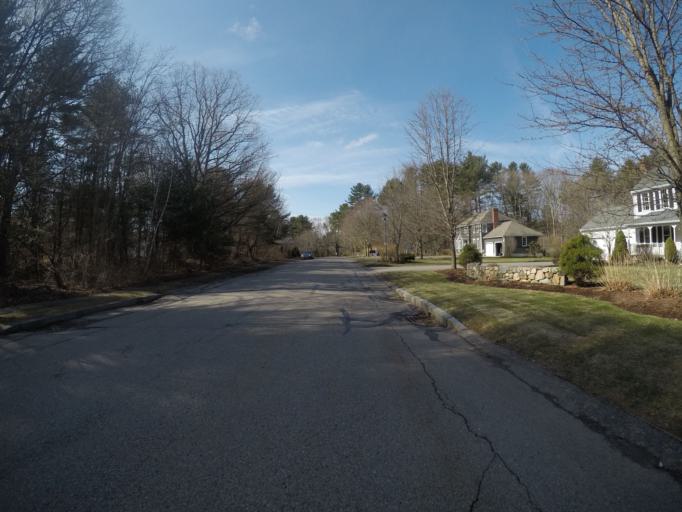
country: US
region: Massachusetts
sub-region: Bristol County
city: Easton
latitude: 42.0166
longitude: -71.1634
